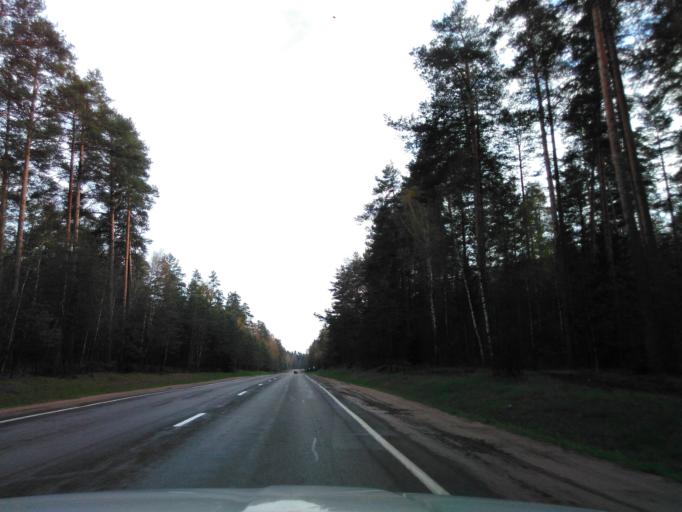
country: BY
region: Minsk
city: Plyeshchanitsy
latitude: 54.3635
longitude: 27.8839
